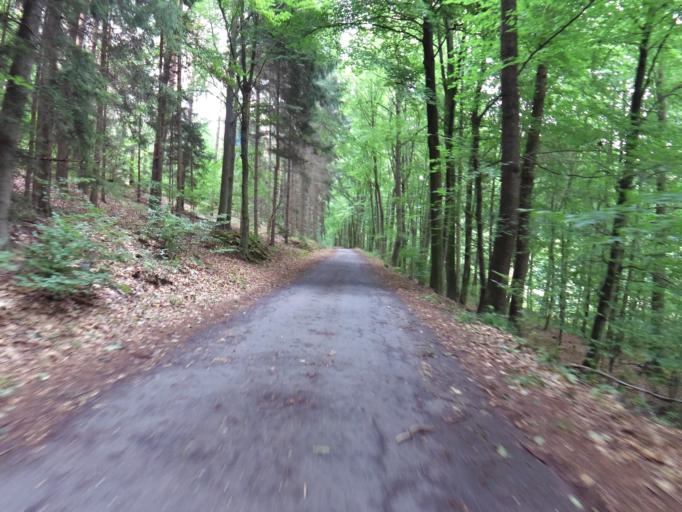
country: DE
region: Hesse
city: Hochst im Odenwald
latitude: 49.7807
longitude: 8.9686
